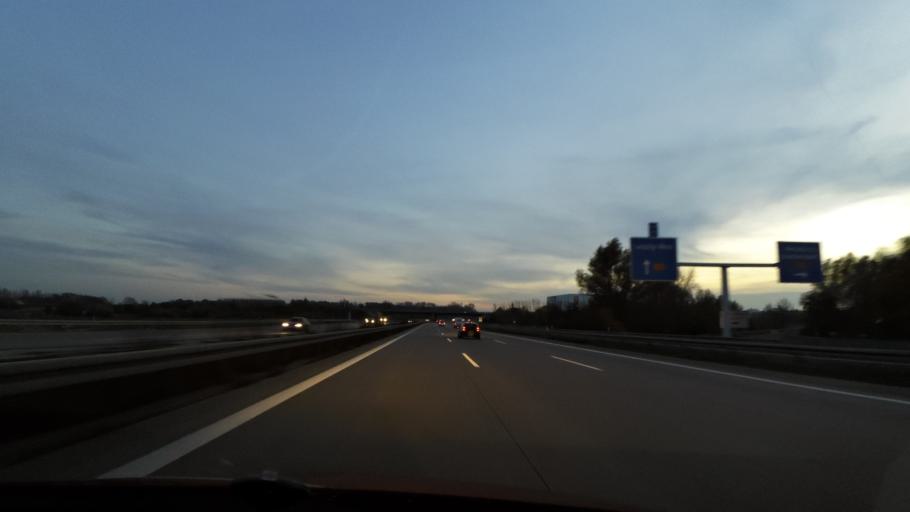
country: DE
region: Saxony-Anhalt
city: Gunthersdorf
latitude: 51.3496
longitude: 12.1870
